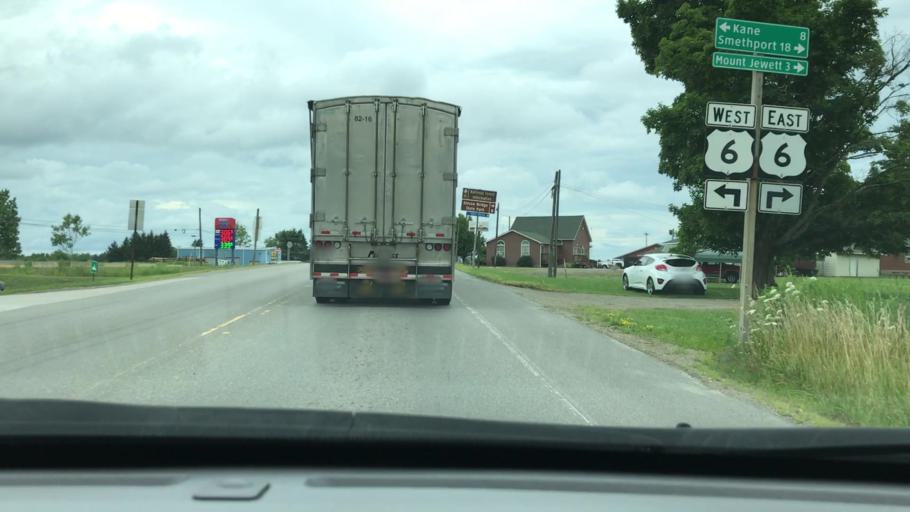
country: US
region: Pennsylvania
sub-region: McKean County
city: Kane
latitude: 41.7071
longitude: -78.6937
